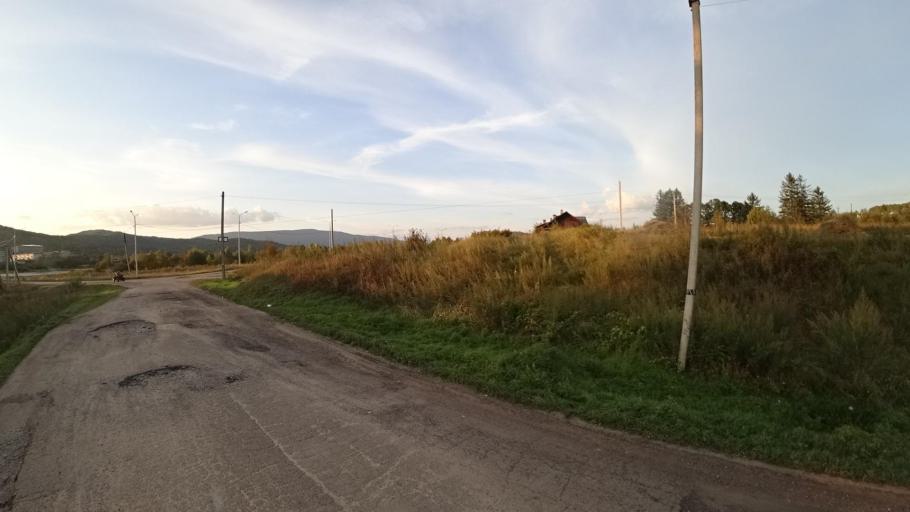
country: RU
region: Jewish Autonomous Oblast
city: Kul'dur
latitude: 49.1985
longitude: 131.6327
